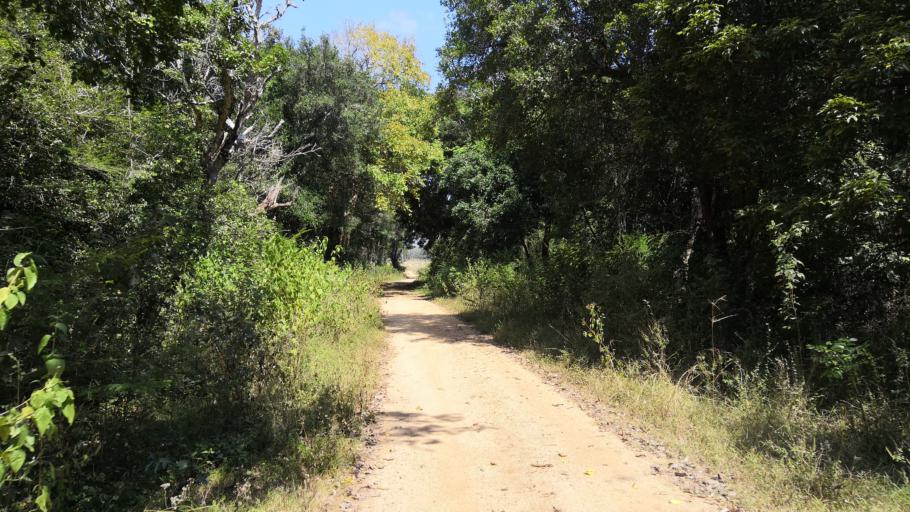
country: LK
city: Padaviya Divisional Secretariat
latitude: 8.9610
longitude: 80.6948
